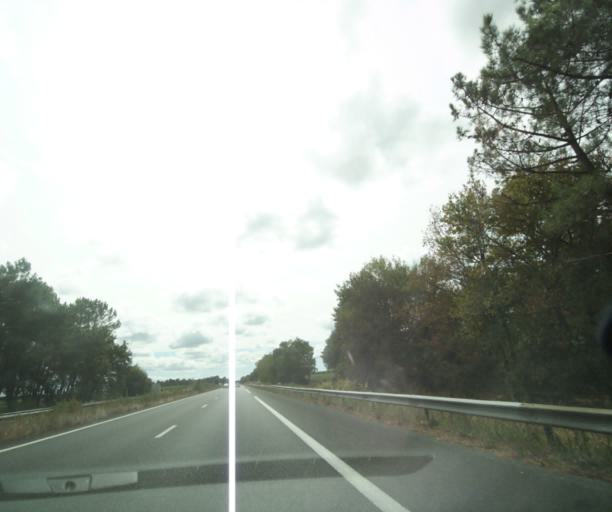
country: FR
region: Aquitaine
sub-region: Departement de la Gironde
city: Marcillac
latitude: 45.2474
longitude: -0.5374
